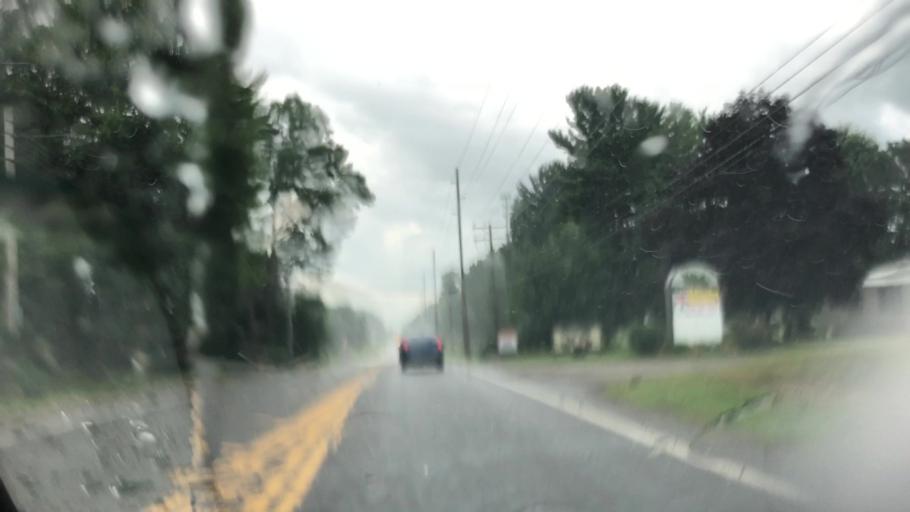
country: US
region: Ohio
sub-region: Stark County
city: Massillon
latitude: 40.8363
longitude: -81.5022
